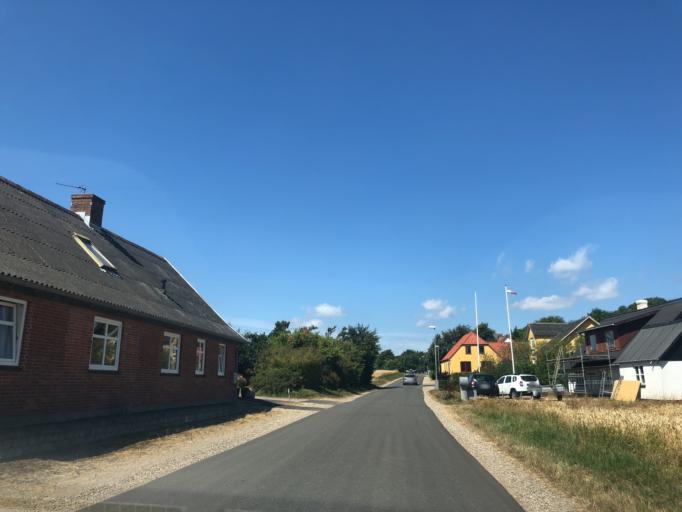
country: DK
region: North Denmark
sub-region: Morso Kommune
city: Nykobing Mors
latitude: 56.8216
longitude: 8.9987
